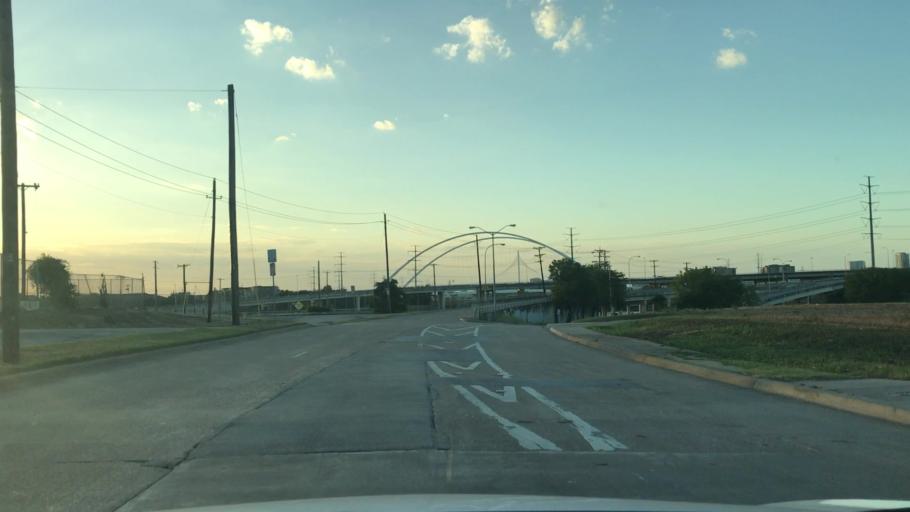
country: US
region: Texas
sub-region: Dallas County
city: Dallas
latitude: 32.7593
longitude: -96.8124
